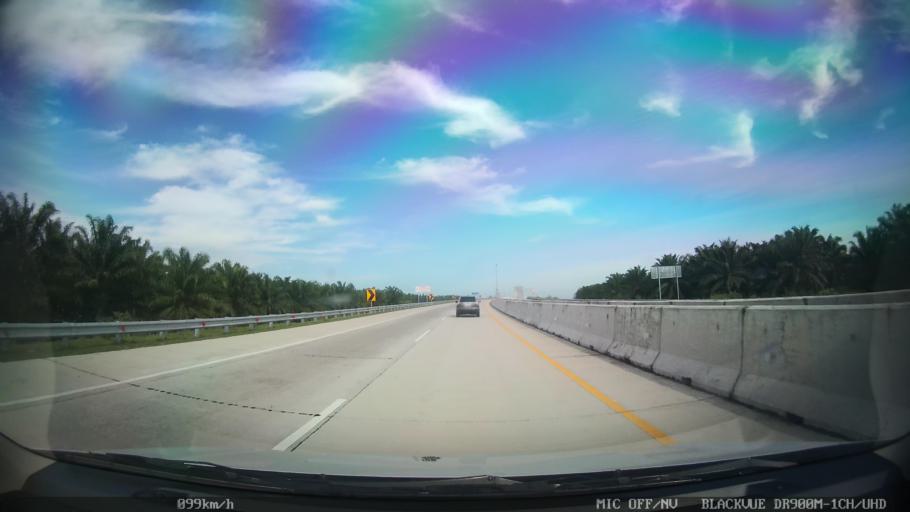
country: ID
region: North Sumatra
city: Binjai
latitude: 3.6504
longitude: 98.5393
